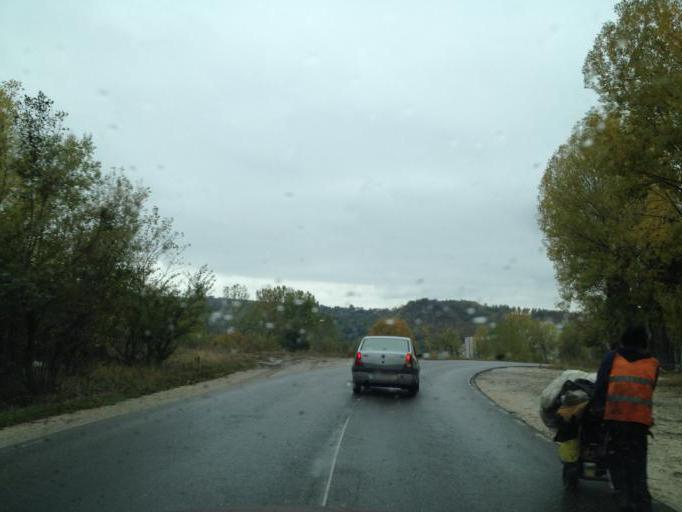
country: RO
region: Arges
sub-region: Comuna Valea Mare-Pravat
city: Valea Mare Pravat
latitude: 45.2911
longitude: 25.1195
